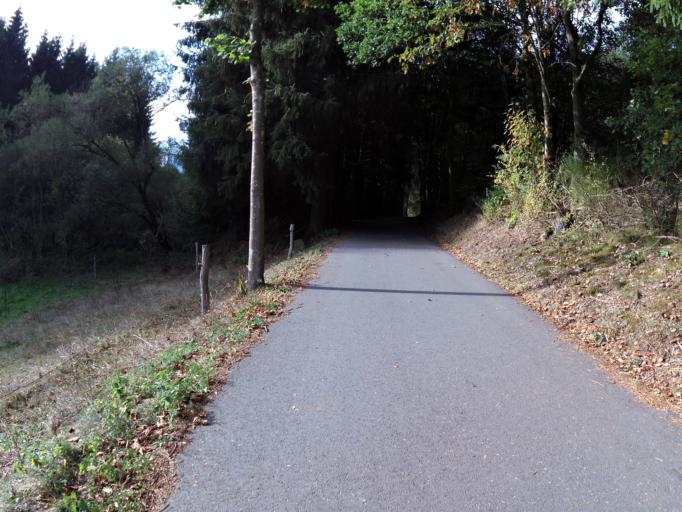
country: BE
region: Wallonia
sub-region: Province de Liege
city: Saint-Vith
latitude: 50.2473
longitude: 6.1476
